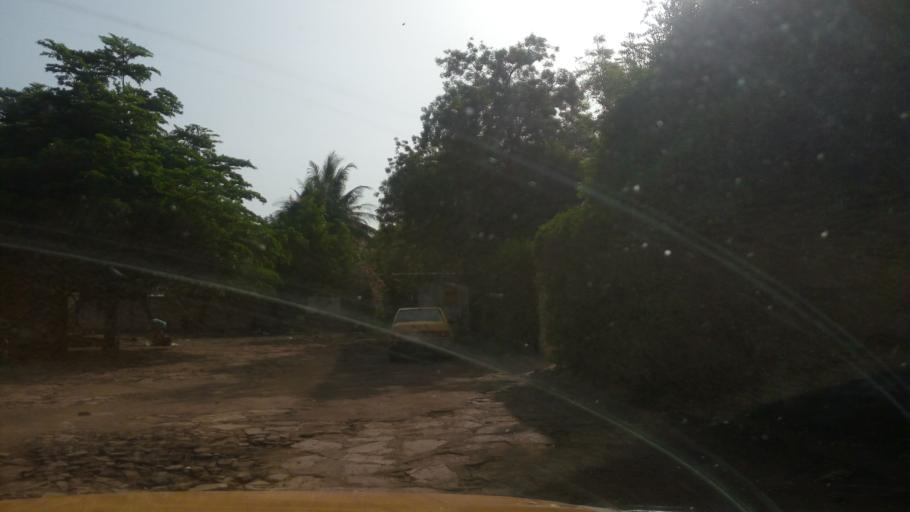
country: ML
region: Bamako
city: Bamako
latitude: 12.6095
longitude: -8.0086
